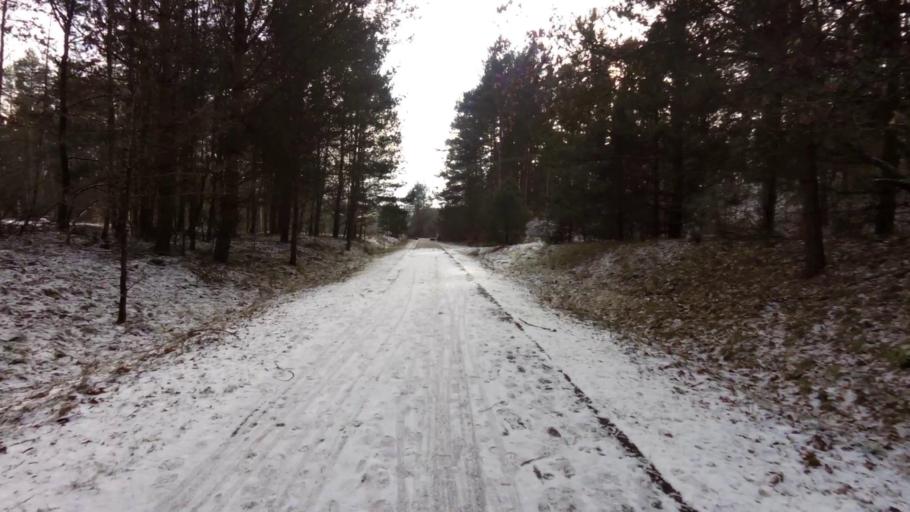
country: PL
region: West Pomeranian Voivodeship
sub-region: Powiat drawski
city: Zlocieniec
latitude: 53.5506
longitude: 16.0201
